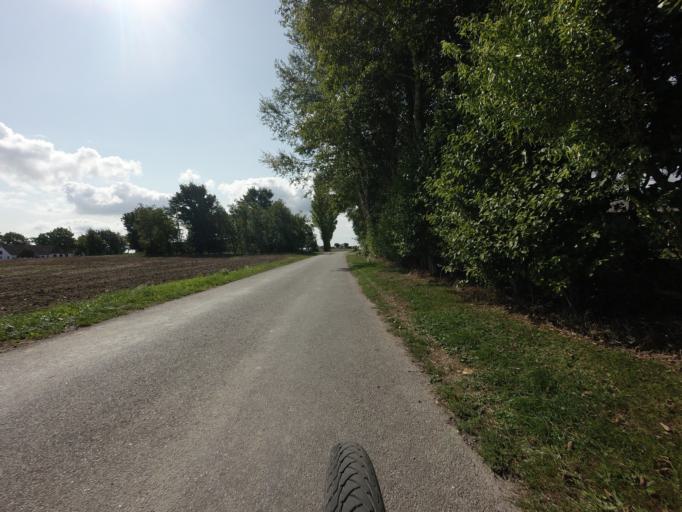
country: DK
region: Zealand
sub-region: Vordingborg Kommune
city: Stege
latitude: 54.9669
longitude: 12.3393
